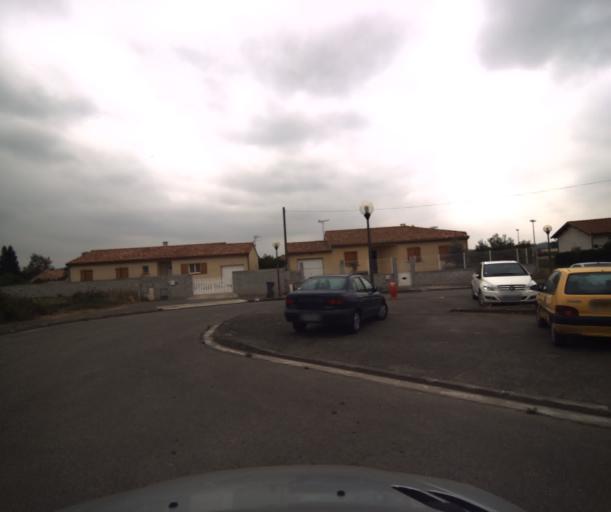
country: FR
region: Midi-Pyrenees
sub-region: Departement de la Haute-Garonne
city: Portet-sur-Garonne
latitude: 43.5313
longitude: 1.4075
